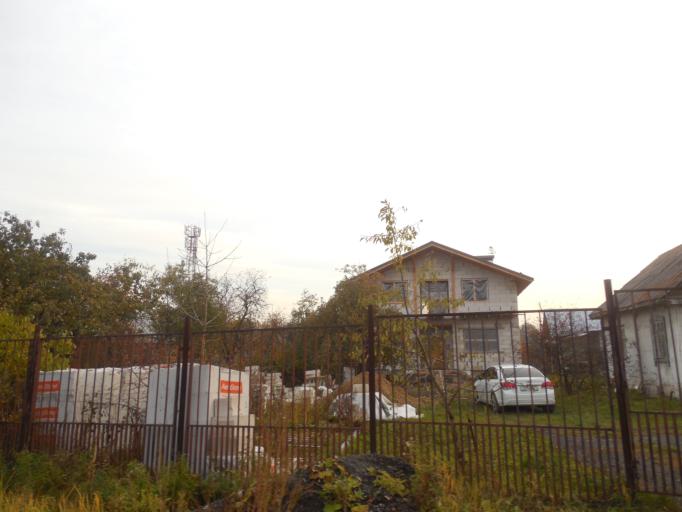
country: RU
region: Moskovskaya
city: Shcherbinka
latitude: 55.4988
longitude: 37.5918
